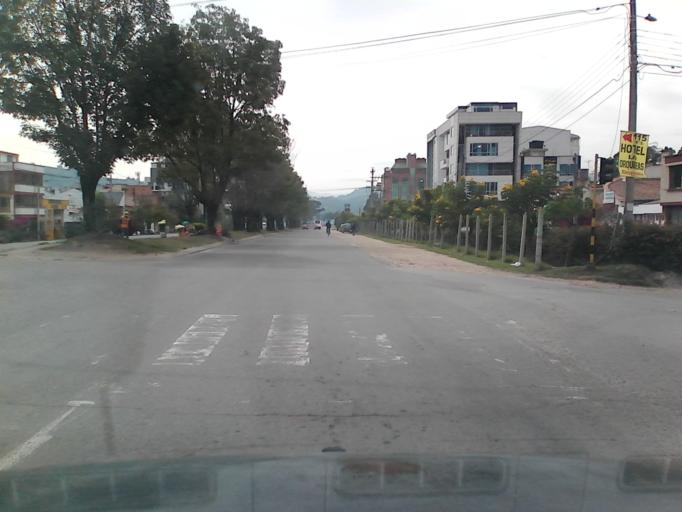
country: CO
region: Boyaca
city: Duitama
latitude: 5.8113
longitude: -73.0301
